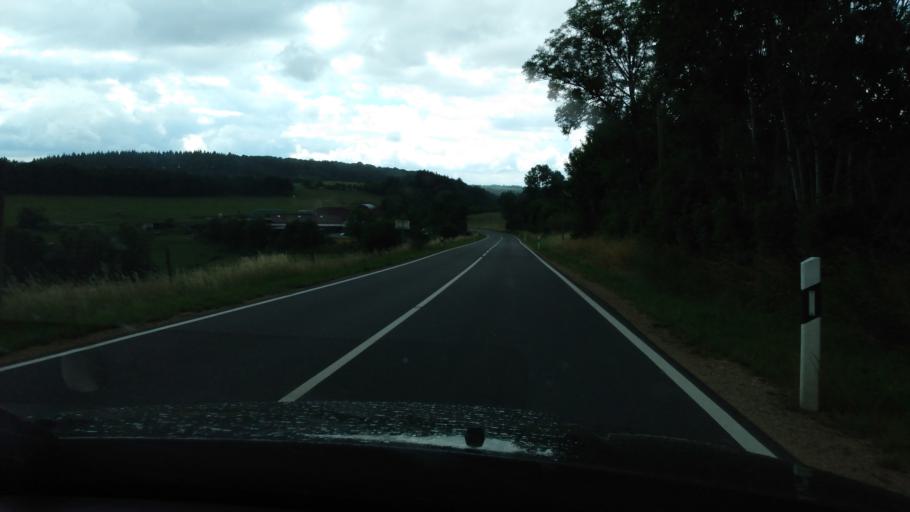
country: DE
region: Rheinland-Pfalz
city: Udersdorf
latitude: 50.1480
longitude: 6.8009
